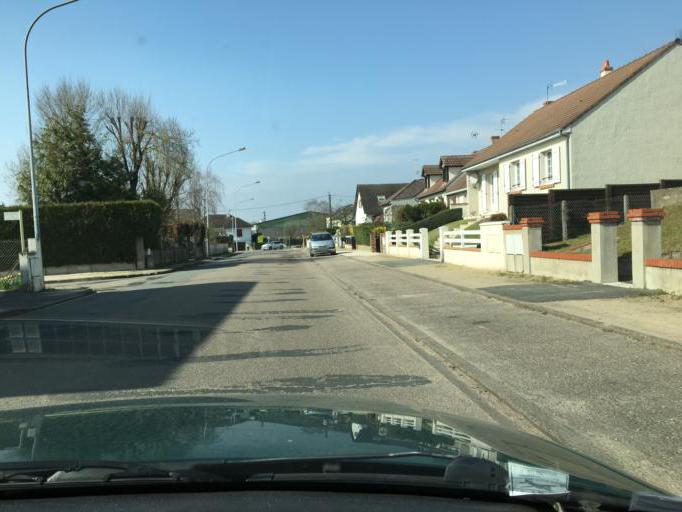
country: FR
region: Centre
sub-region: Departement du Loiret
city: Fleury-les-Aubrais
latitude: 47.9416
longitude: 1.9030
